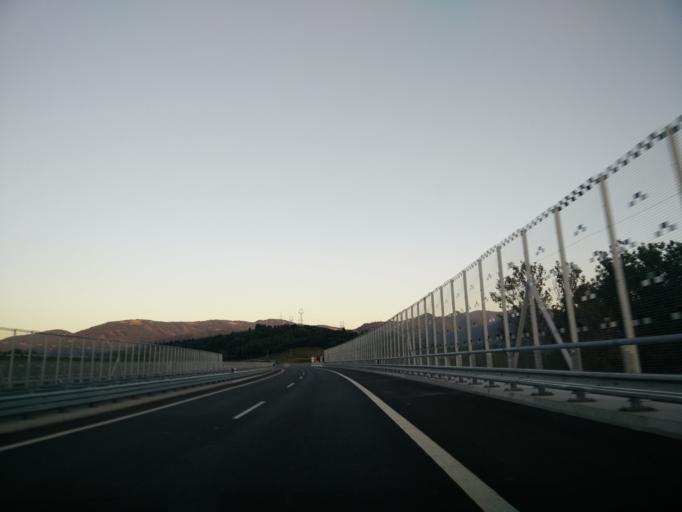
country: SK
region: Zilinsky
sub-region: Okres Martin
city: Martin
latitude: 49.1004
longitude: 19.0197
